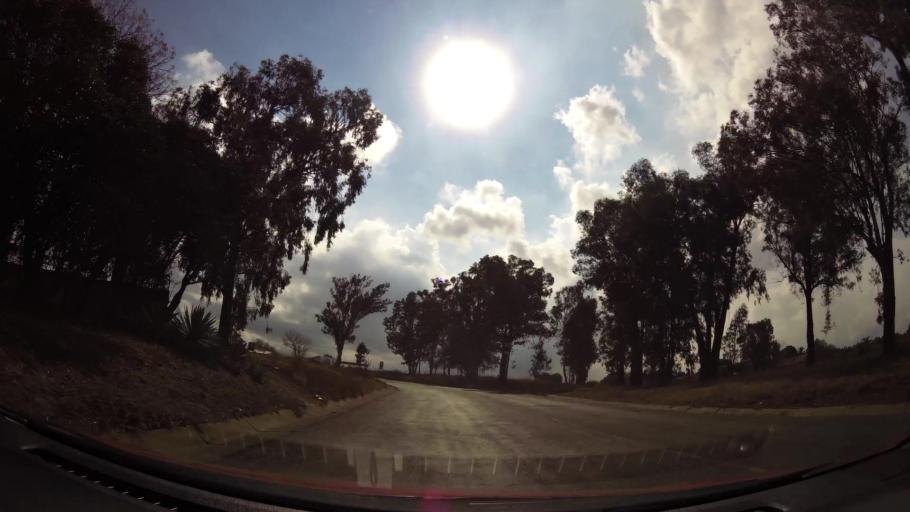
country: ZA
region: Gauteng
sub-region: Sedibeng District Municipality
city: Vanderbijlpark
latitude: -26.7414
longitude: 27.8232
